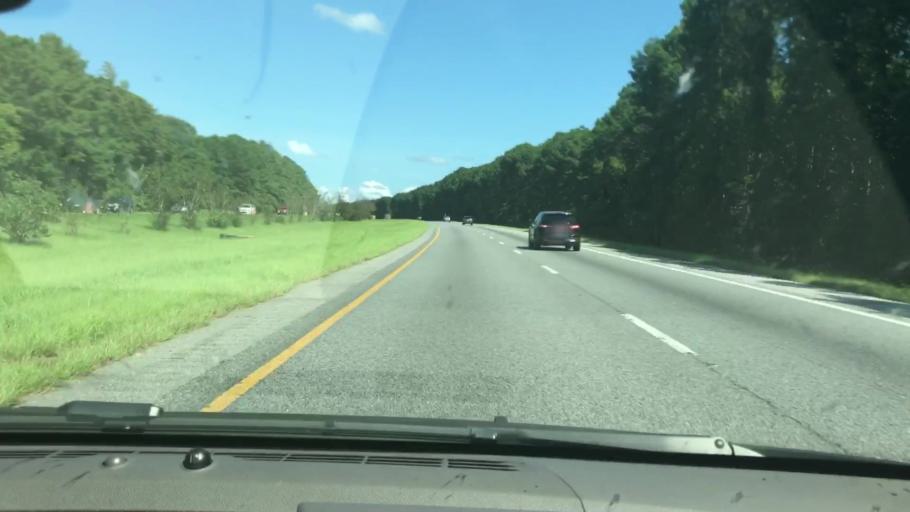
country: US
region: Georgia
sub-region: Harris County
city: Hamilton
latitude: 32.6492
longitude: -84.9720
